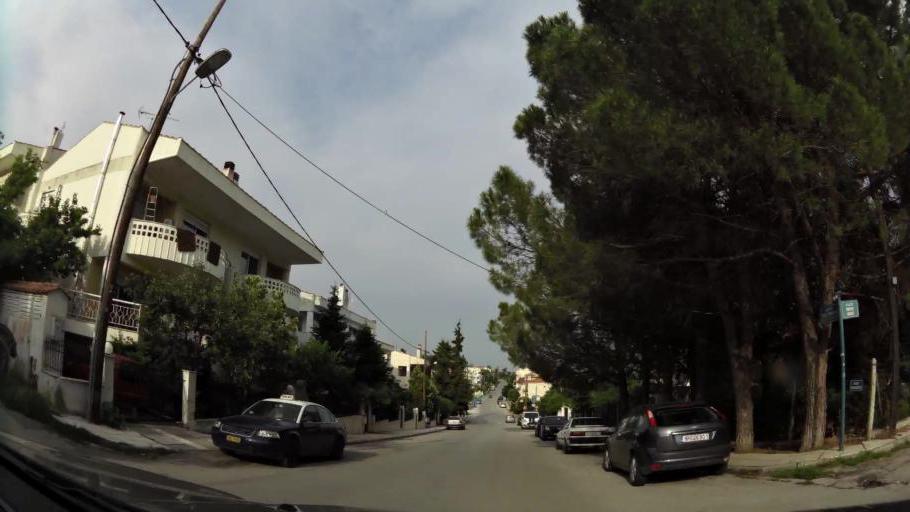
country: GR
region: Central Macedonia
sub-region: Nomos Thessalonikis
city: Oraiokastro
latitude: 40.7253
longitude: 22.9183
